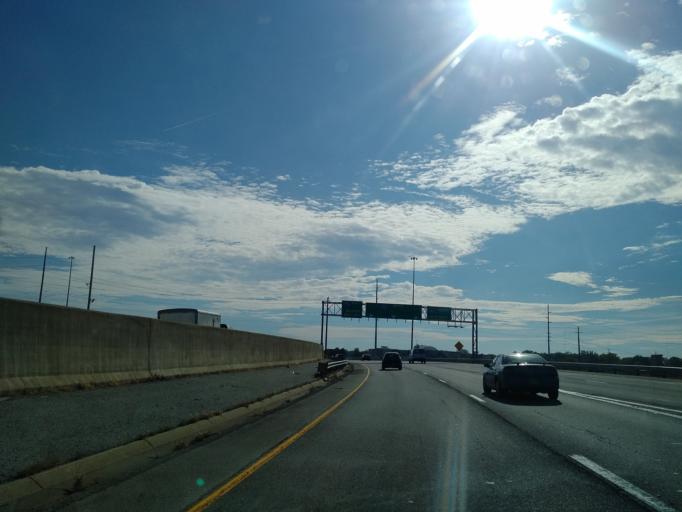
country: US
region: Indiana
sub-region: Marion County
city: Warren Park
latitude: 39.7988
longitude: -86.0473
